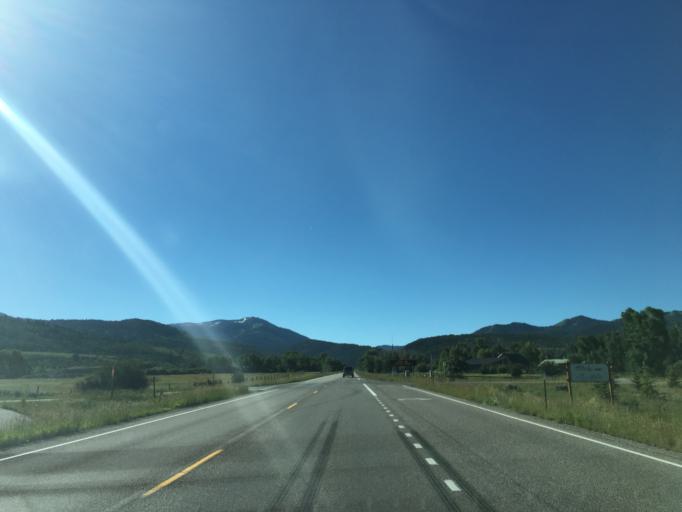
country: US
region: Idaho
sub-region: Teton County
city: Victor
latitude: 43.5906
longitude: -111.1022
